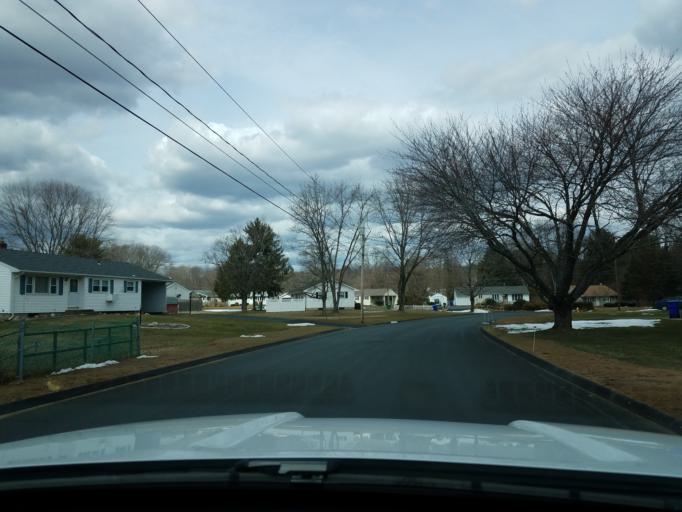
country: US
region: Connecticut
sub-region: Hartford County
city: Manchester
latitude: 41.8252
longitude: -72.5172
